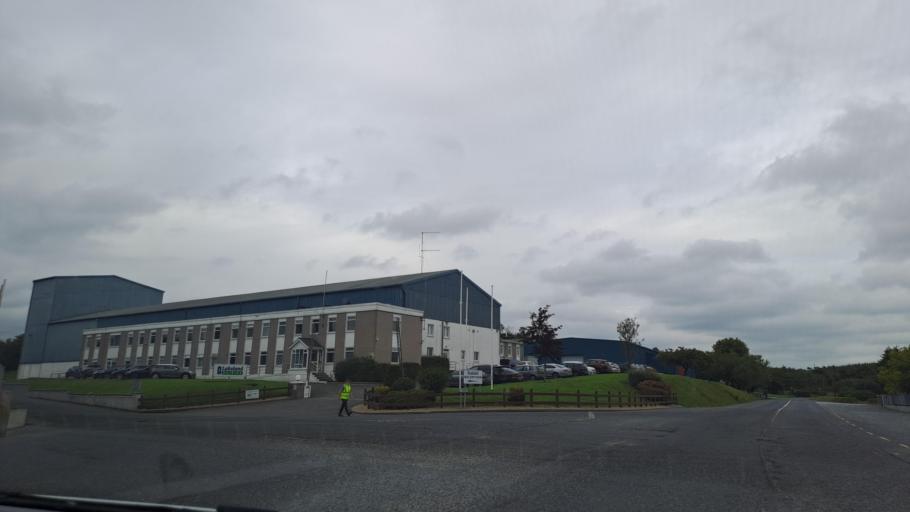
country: IE
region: Ulster
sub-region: An Cabhan
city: Bailieborough
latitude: 53.9273
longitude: -6.9701
